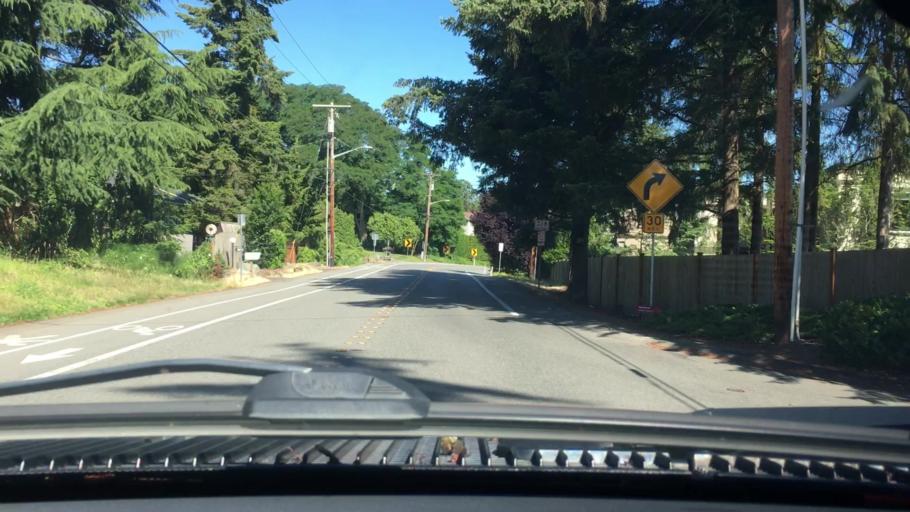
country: US
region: Washington
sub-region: King County
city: Sammamish
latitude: 47.6439
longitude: -122.1065
